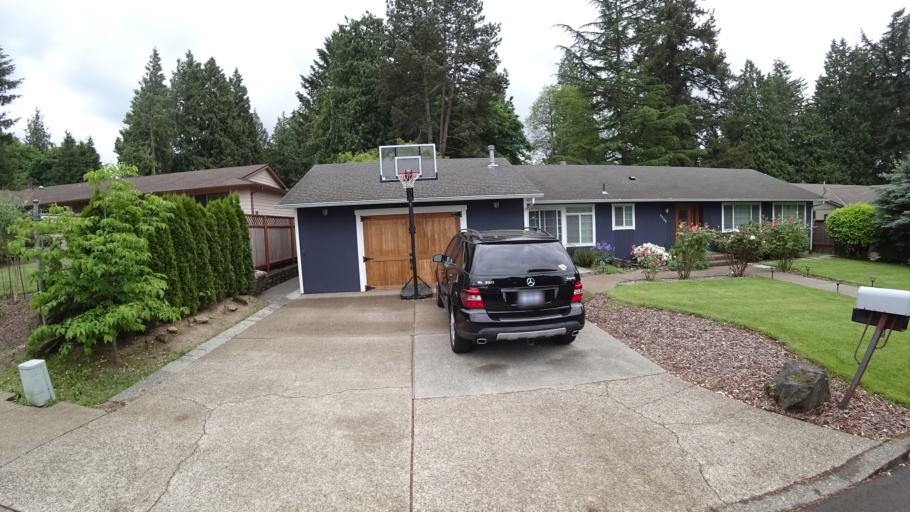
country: US
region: Oregon
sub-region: Washington County
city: Garden Home-Whitford
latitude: 45.4638
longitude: -122.7699
